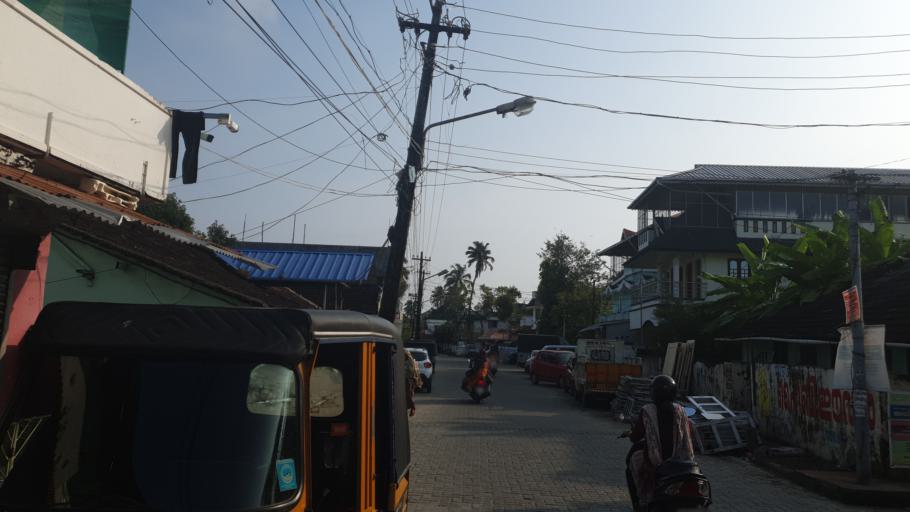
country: IN
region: Kerala
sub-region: Ernakulam
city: Cochin
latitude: 9.9624
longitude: 76.2522
